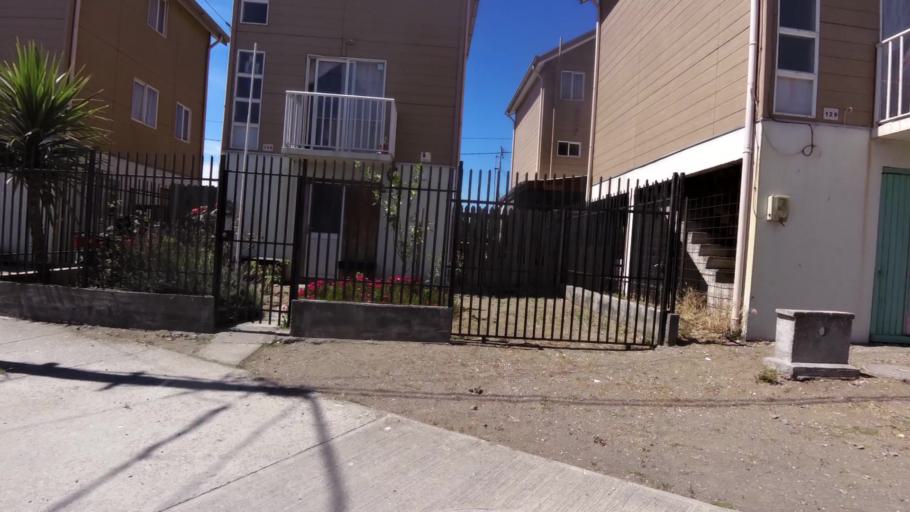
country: CL
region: Biobio
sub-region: Provincia de Concepcion
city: Talcahuano
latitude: -36.7260
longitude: -73.1050
